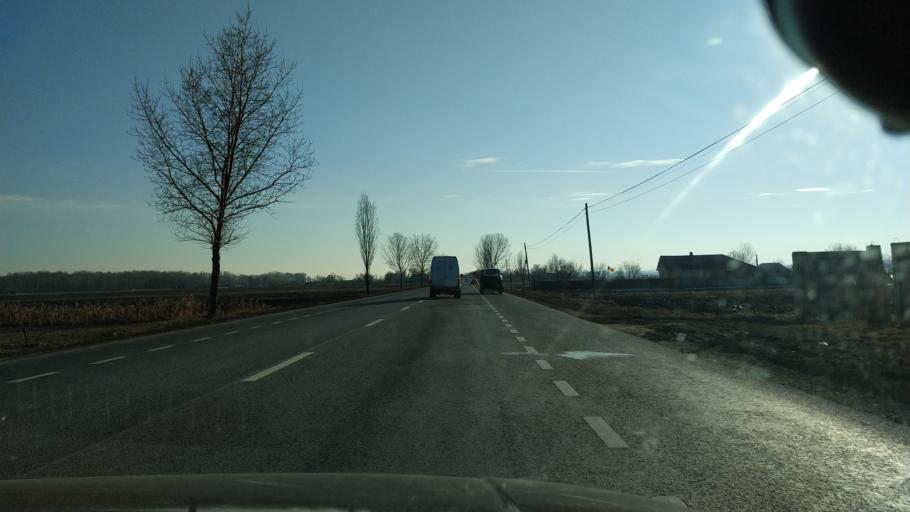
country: RO
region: Neamt
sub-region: Comuna Icusesti
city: Icusesti
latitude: 46.8095
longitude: 26.8864
